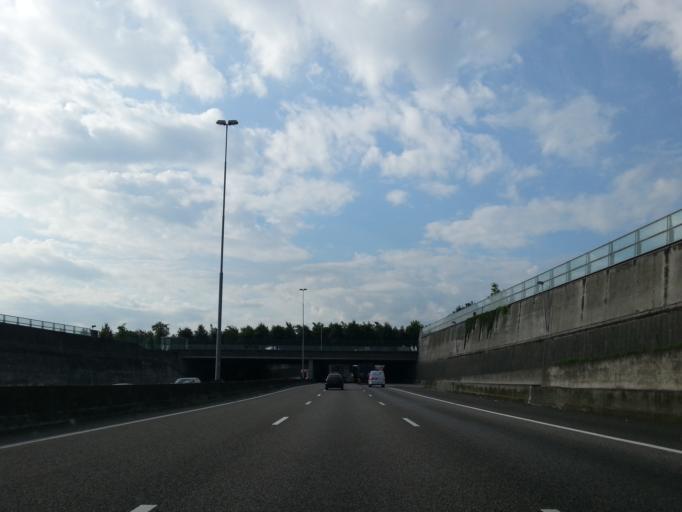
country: NL
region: North Brabant
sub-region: Gemeente Breda
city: Breda
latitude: 51.6006
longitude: 4.7220
